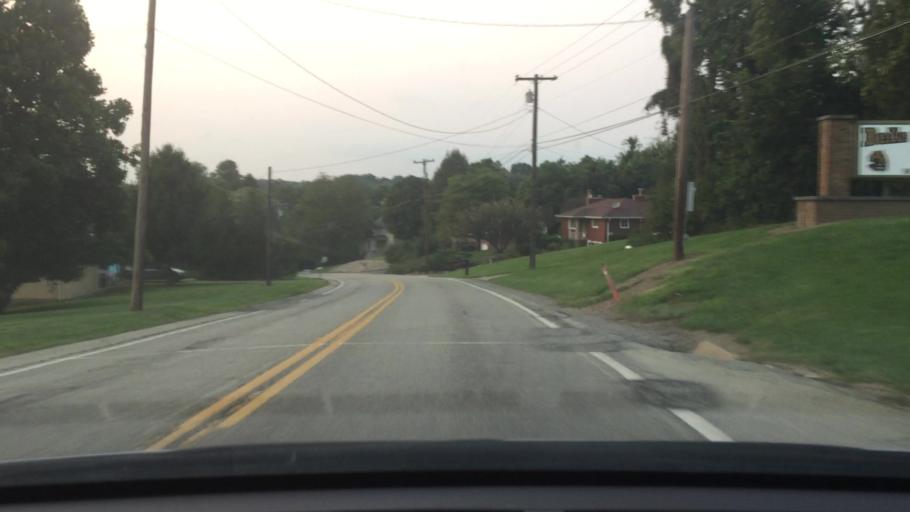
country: US
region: Pennsylvania
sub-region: Westmoreland County
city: Fellsburg
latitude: 40.1754
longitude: -79.8207
